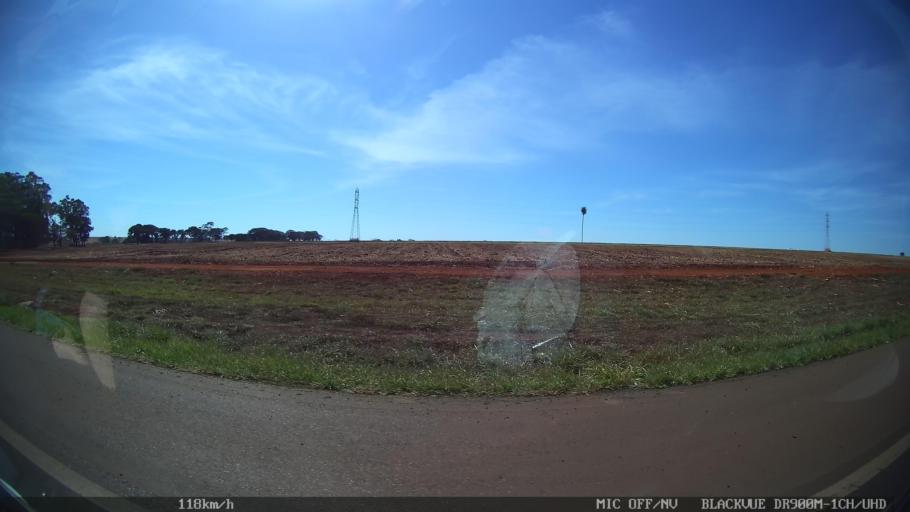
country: BR
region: Sao Paulo
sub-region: Ipua
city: Ipua
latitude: -20.4615
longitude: -48.1404
